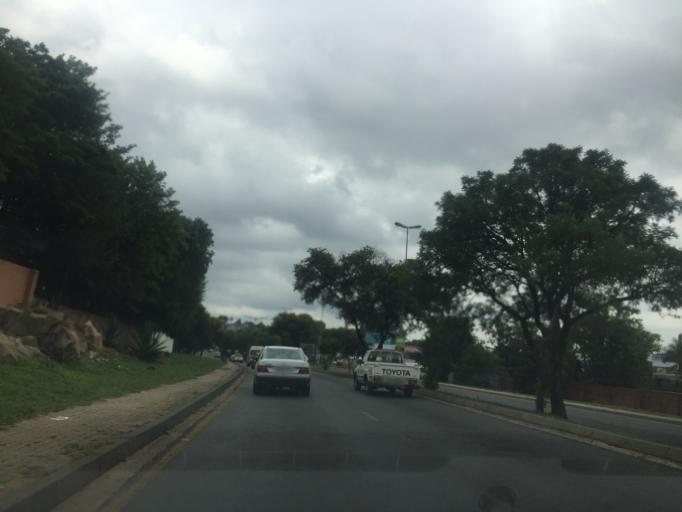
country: ZA
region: Gauteng
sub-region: City of Johannesburg Metropolitan Municipality
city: Roodepoort
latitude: -26.0848
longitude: 27.9793
